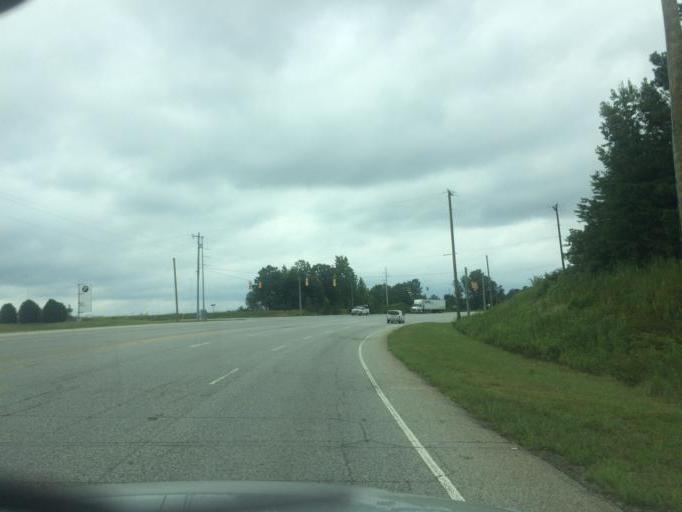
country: US
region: South Carolina
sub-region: Greenville County
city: Greer
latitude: 34.8999
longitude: -82.1934
